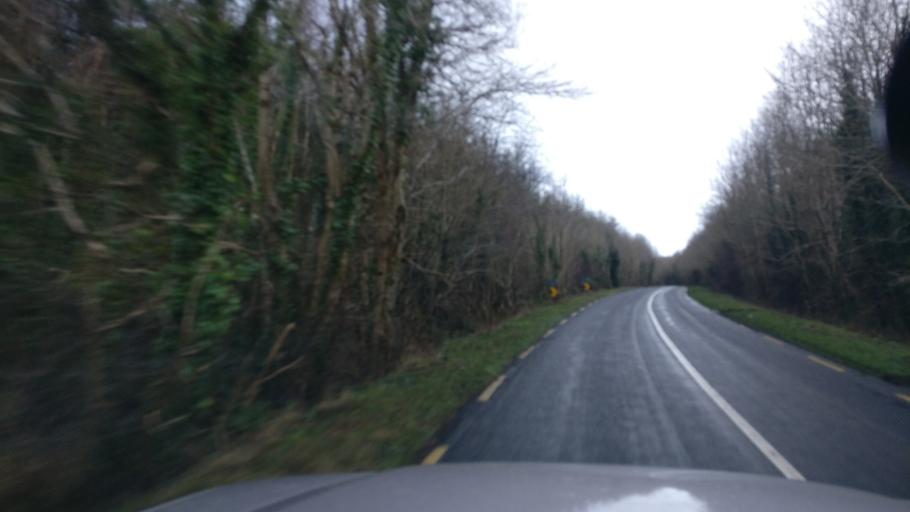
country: IE
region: Connaught
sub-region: County Galway
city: Athenry
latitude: 53.2967
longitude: -8.6579
